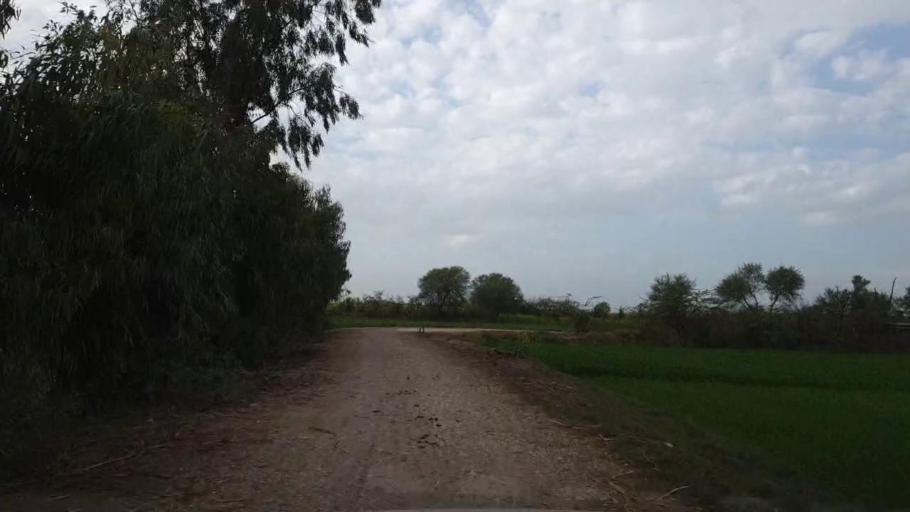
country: PK
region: Sindh
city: Tando Adam
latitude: 25.6587
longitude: 68.6105
